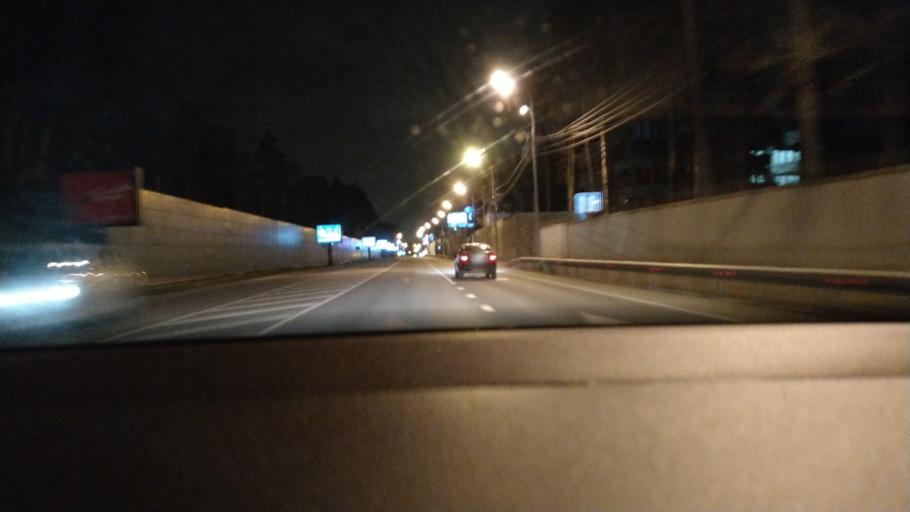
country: RU
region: Moskovskaya
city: Barvikha
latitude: 55.7444
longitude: 37.2859
